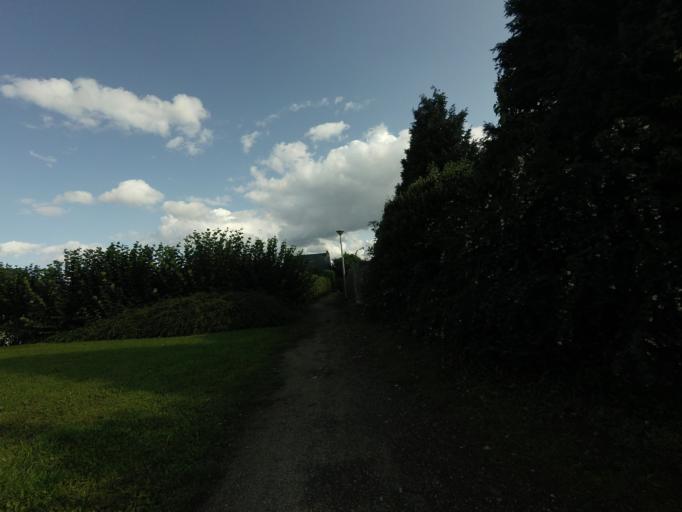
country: BE
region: Flanders
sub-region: Provincie Vlaams-Brabant
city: Londerzeel
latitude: 50.9867
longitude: 4.3260
